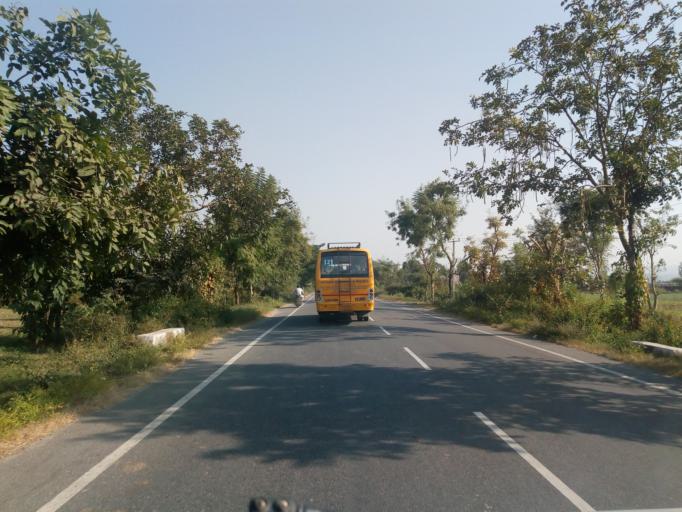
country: IN
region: Uttarakhand
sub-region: Dehradun
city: Harbatpur
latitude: 30.4141
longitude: 77.7854
